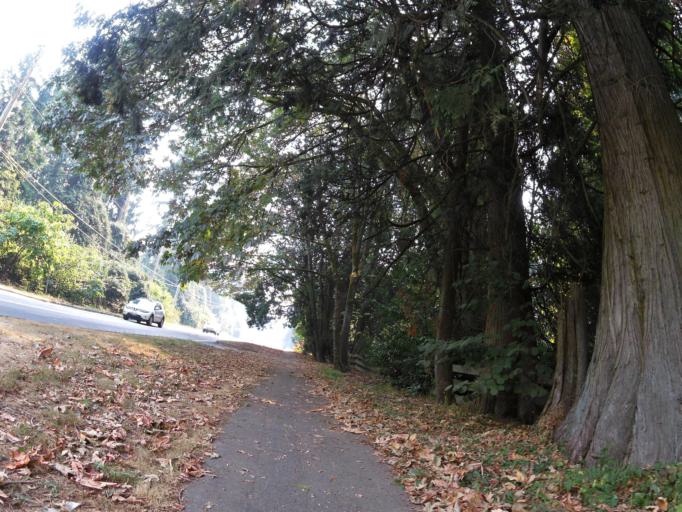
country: CA
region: British Columbia
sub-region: Greater Vancouver Regional District
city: White Rock
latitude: 49.0581
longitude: -122.7570
